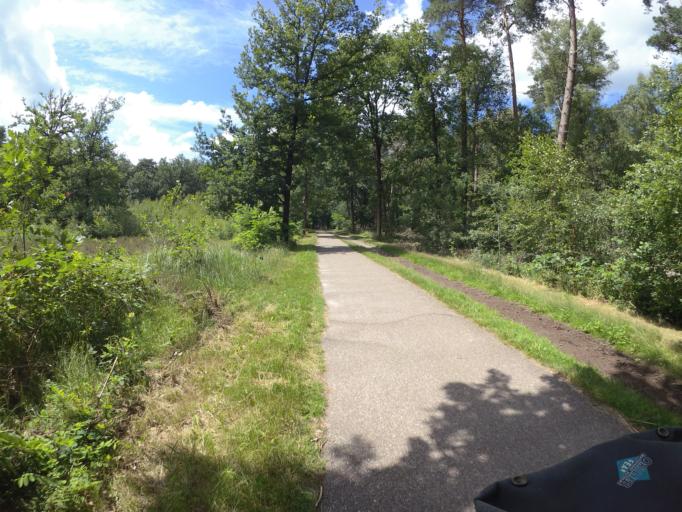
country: NL
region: North Brabant
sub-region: Gemeente Oisterwijk
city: Oisterwijk
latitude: 51.5610
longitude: 5.1933
